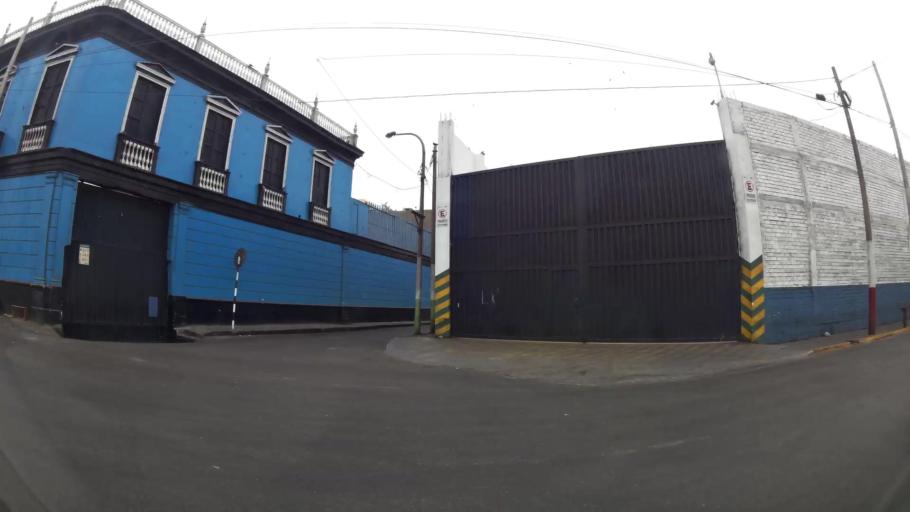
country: PE
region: Callao
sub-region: Callao
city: Callao
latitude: -12.0560
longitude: -77.1438
